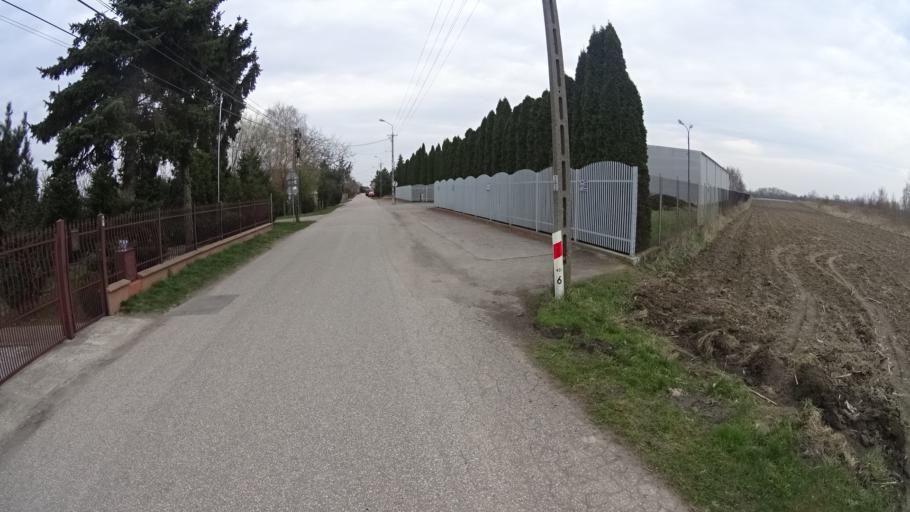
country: PL
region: Masovian Voivodeship
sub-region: Powiat warszawski zachodni
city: Jozefow
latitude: 52.2074
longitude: 20.6665
